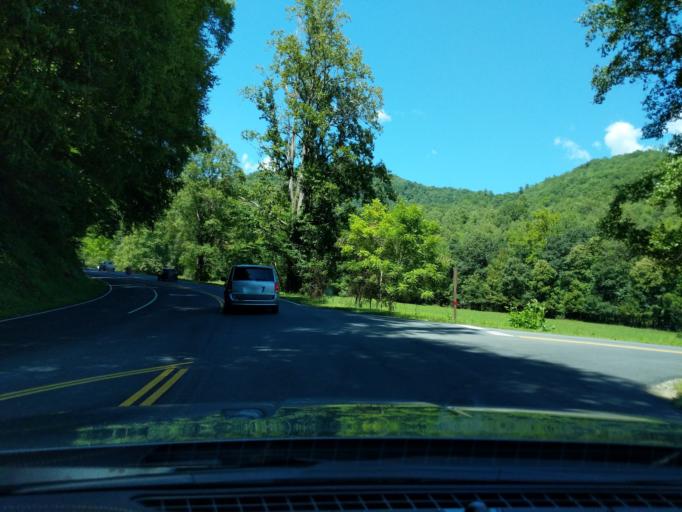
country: US
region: North Carolina
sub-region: Swain County
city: Cherokee
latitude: 35.5411
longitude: -83.2988
